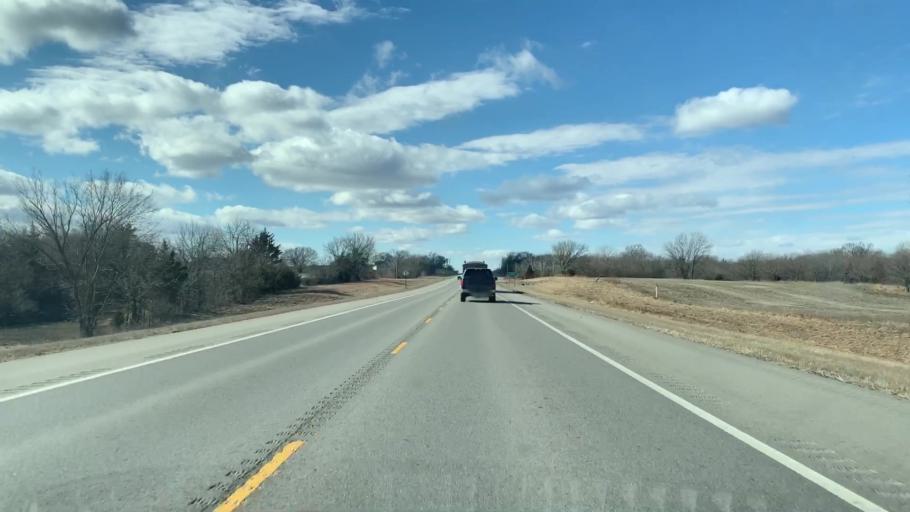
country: US
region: Kansas
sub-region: Cherokee County
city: Columbus
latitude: 37.3399
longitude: -94.8880
